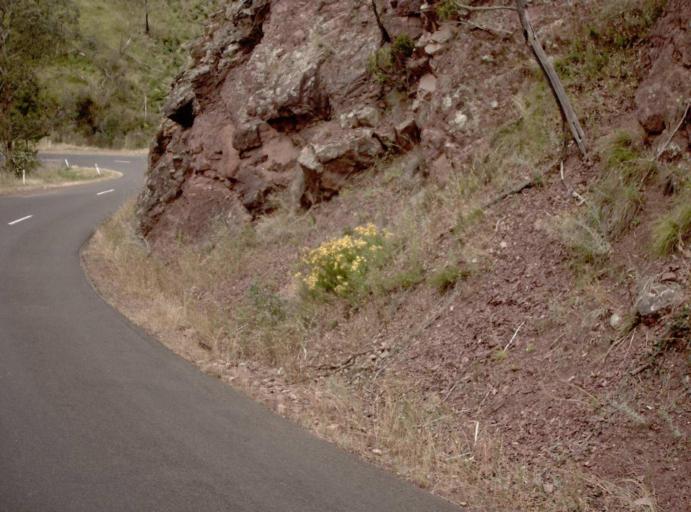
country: AU
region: Victoria
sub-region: Wellington
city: Heyfield
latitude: -37.7030
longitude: 146.6677
